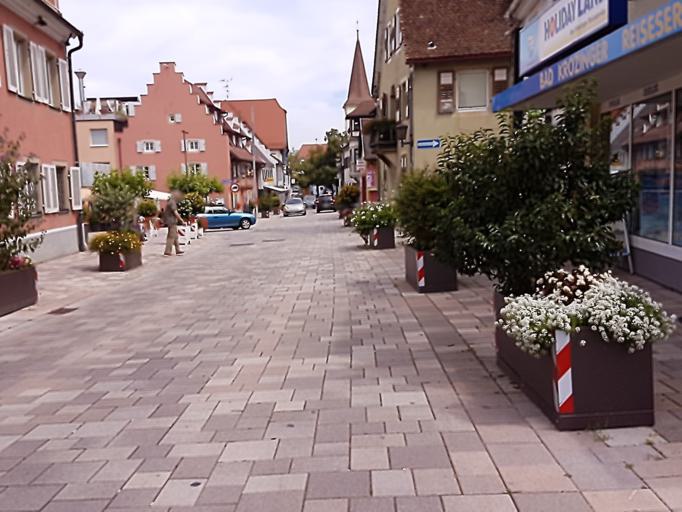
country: DE
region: Baden-Wuerttemberg
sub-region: Freiburg Region
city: Bad Krozingen
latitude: 47.9148
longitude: 7.6986
